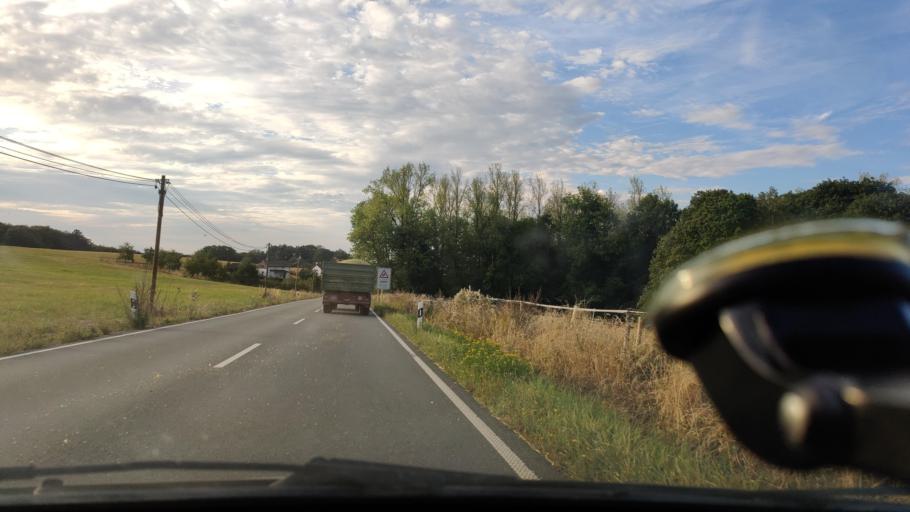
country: DE
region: North Rhine-Westphalia
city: Schwerte
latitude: 51.3817
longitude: 7.5902
